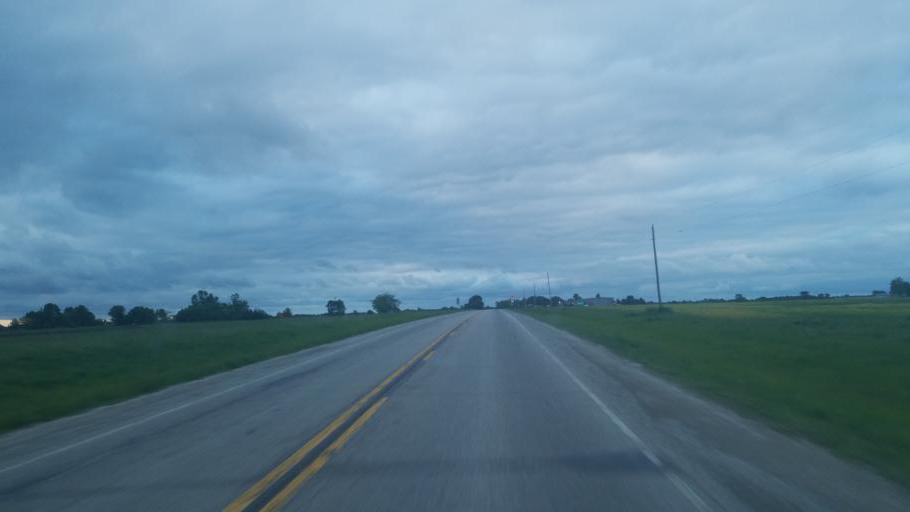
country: US
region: Iowa
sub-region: Decatur County
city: Lamoni
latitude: 40.6015
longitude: -93.9390
